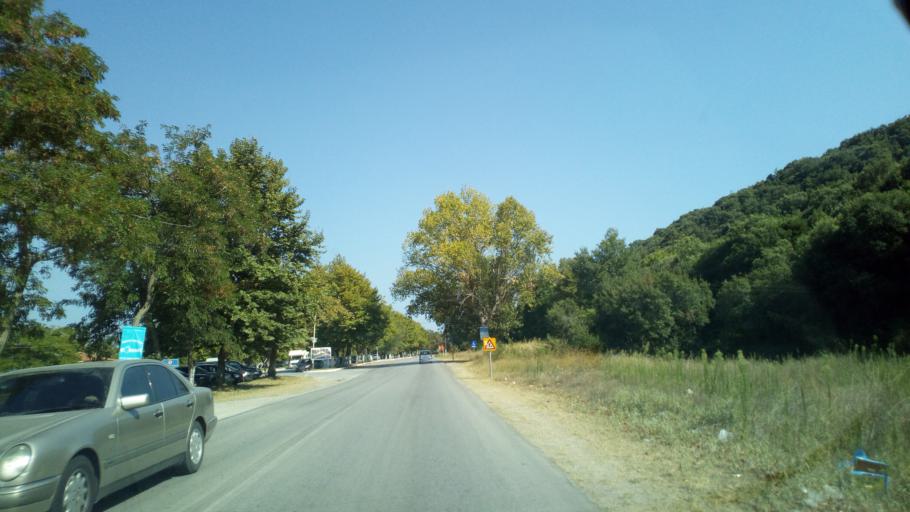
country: GR
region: Central Macedonia
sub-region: Nomos Thessalonikis
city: Stavros
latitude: 40.6633
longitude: 23.7136
